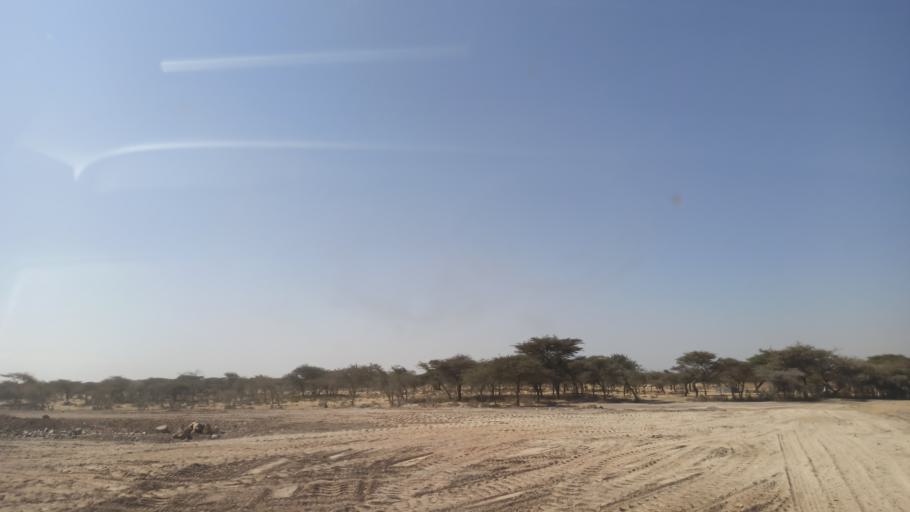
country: ET
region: Oromiya
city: Ziway
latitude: 7.6771
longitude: 38.6766
